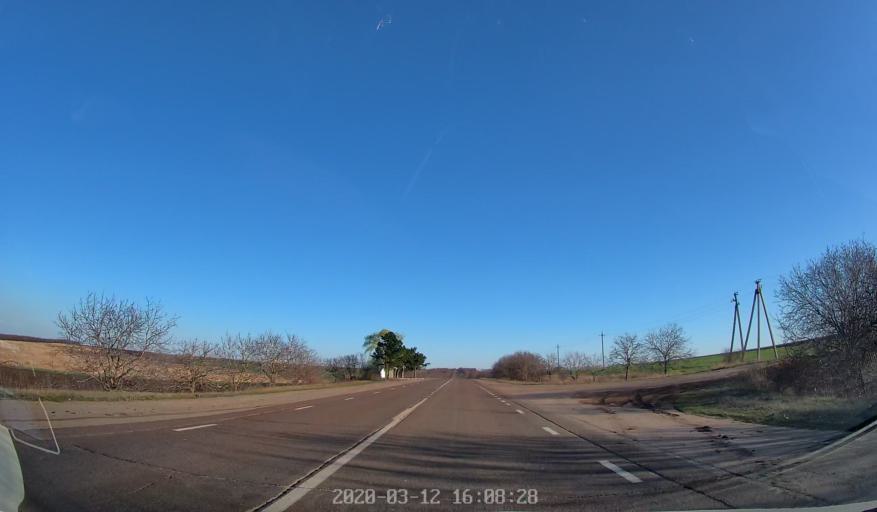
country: MD
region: Anenii Noi
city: Anenii Noi
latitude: 46.9669
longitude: 29.2062
